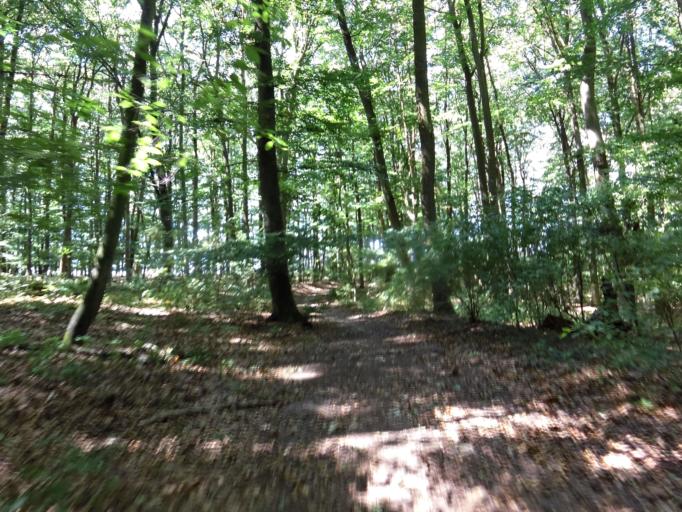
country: DE
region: Bavaria
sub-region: Regierungsbezirk Unterfranken
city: Theilheim
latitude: 49.7497
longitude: 10.0136
